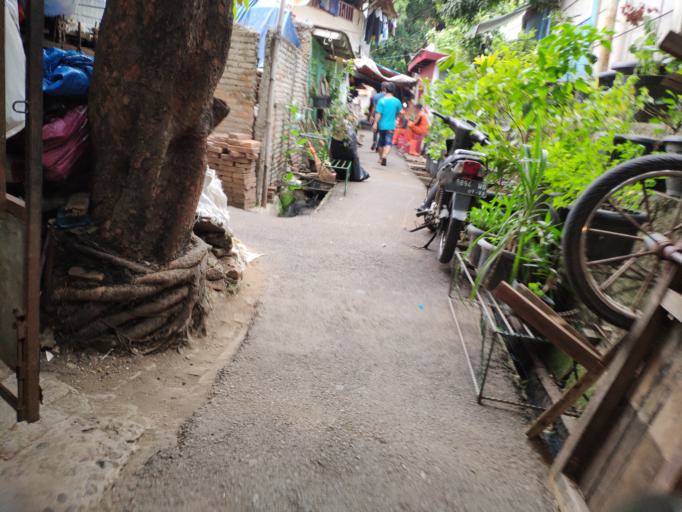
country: ID
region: Jakarta Raya
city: Jakarta
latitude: -6.2109
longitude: 106.8632
